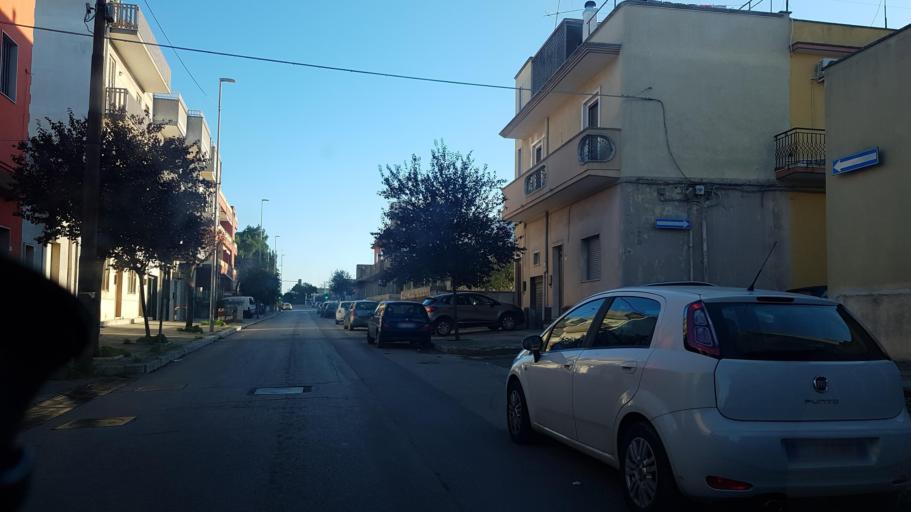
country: IT
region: Apulia
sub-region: Provincia di Brindisi
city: Latiano
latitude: 40.5487
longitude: 17.7190
